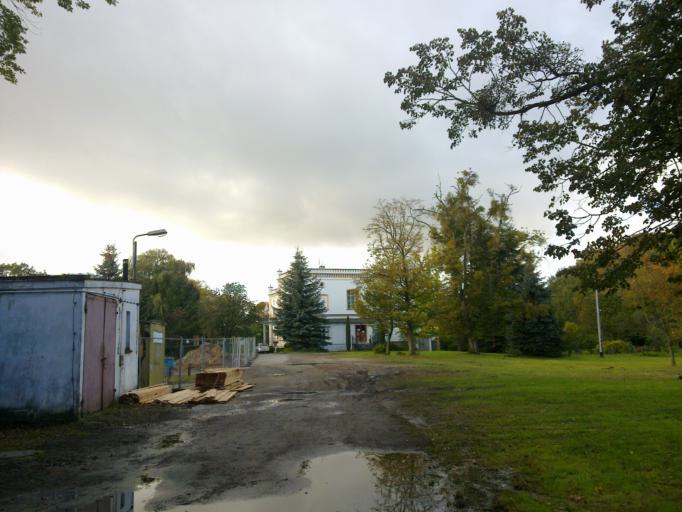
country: PL
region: Warmian-Masurian Voivodeship
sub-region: Powiat elblaski
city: Gronowo Gorne
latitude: 54.1743
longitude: 19.4437
